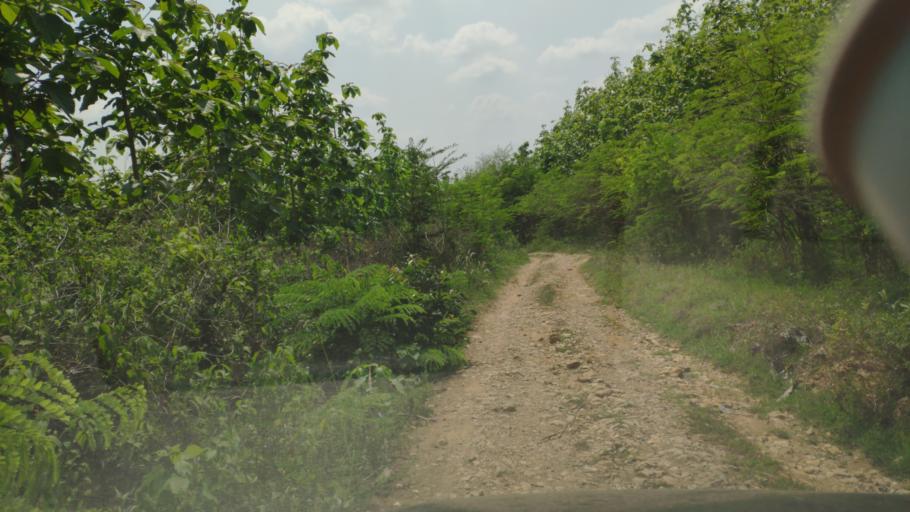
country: ID
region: Central Java
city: Gaplokan
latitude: -6.9098
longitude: 111.2694
